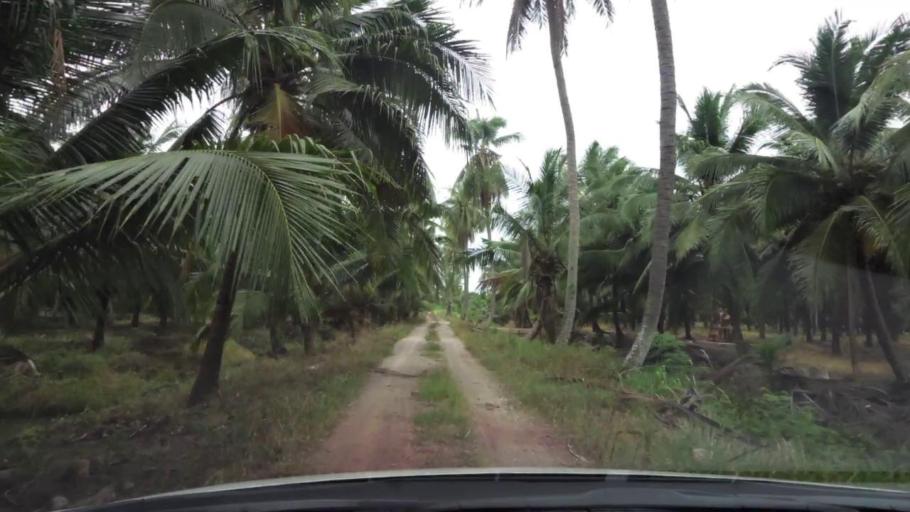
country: TH
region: Samut Sakhon
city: Ban Phaeo
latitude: 13.6123
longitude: 100.0282
